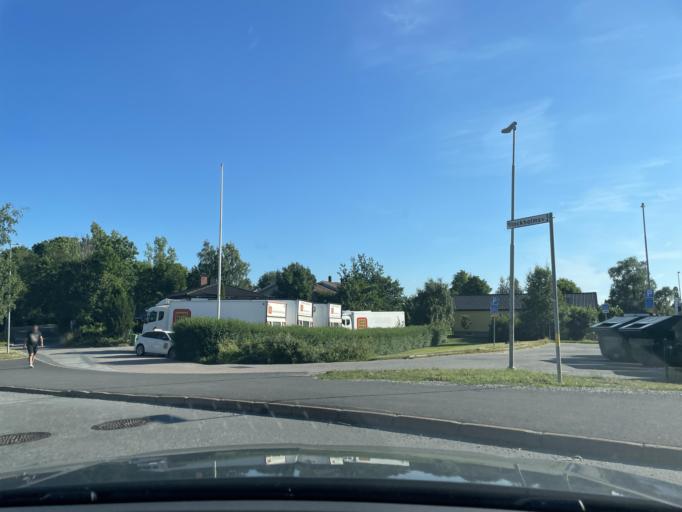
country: SE
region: Stockholm
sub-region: Sigtuna Kommun
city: Marsta
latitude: 59.6242
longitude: 17.8491
